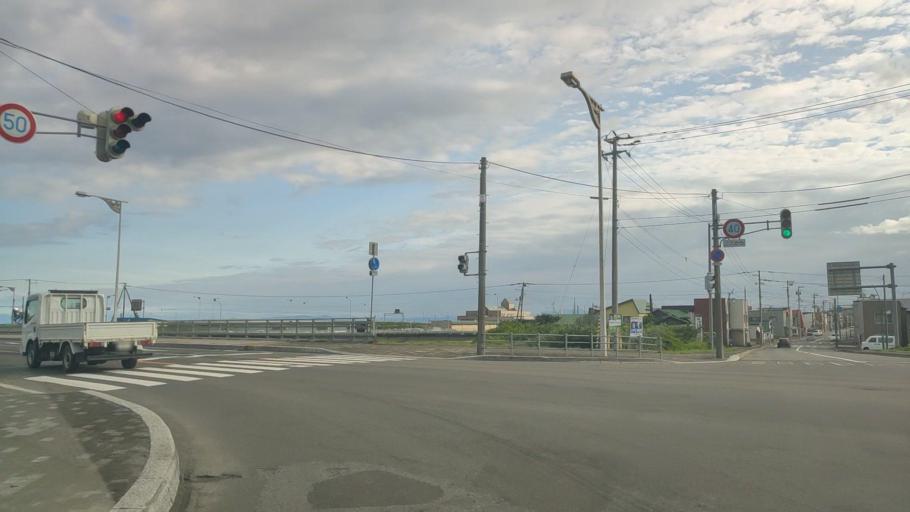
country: JP
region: Hokkaido
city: Niseko Town
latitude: 42.5179
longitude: 140.3814
